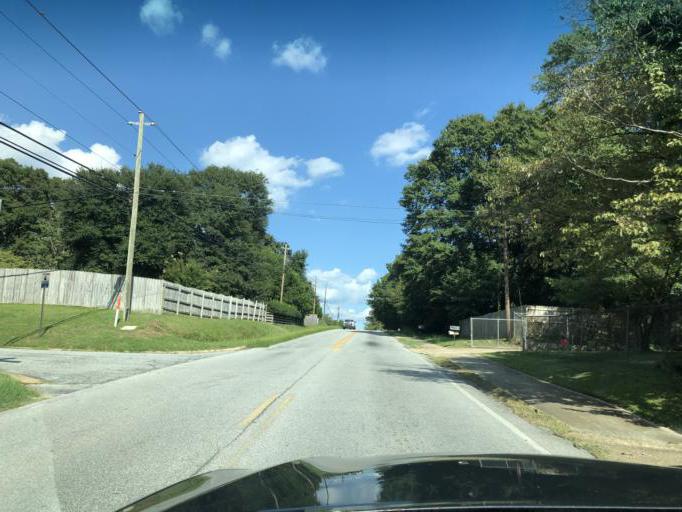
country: US
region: Georgia
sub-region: Muscogee County
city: Columbus
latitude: 32.5395
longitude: -84.9315
